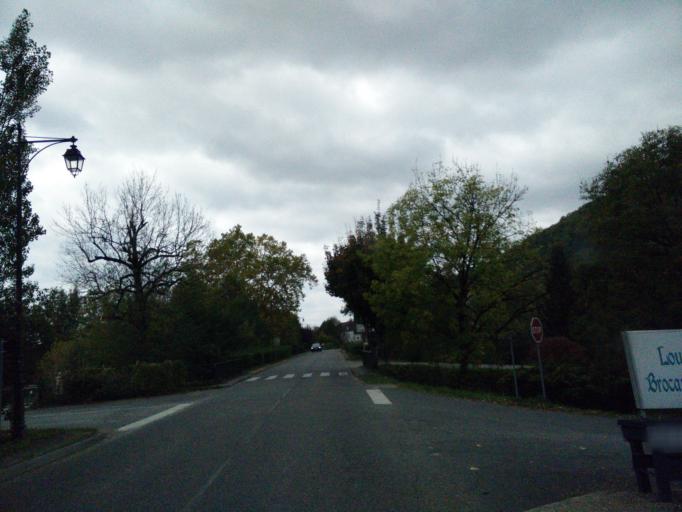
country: FR
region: Midi-Pyrenees
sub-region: Departement du Lot
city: Prayssac
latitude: 44.5029
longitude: 1.2267
